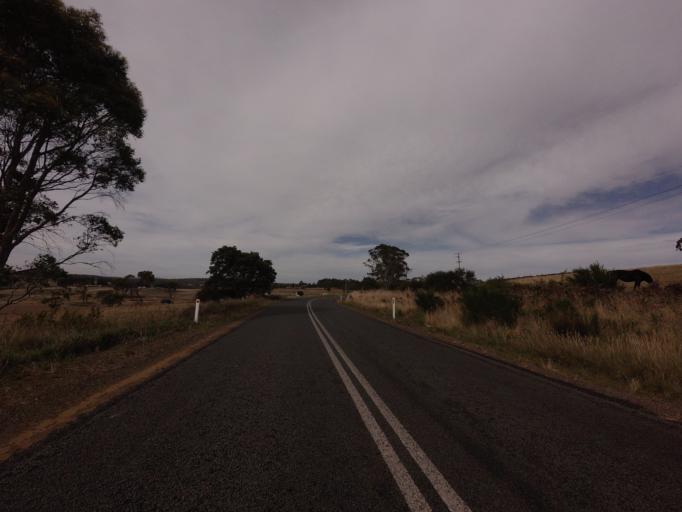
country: AU
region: Tasmania
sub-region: Brighton
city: Bridgewater
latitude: -42.3819
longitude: 147.4244
